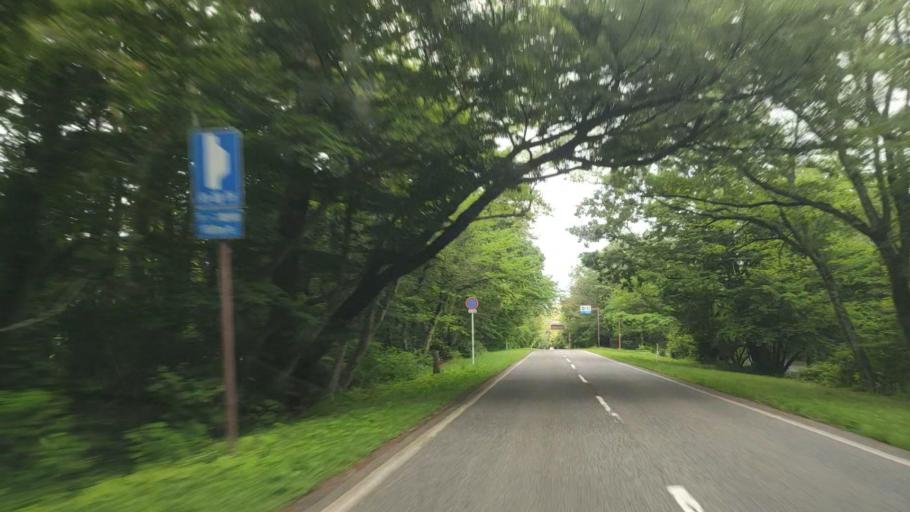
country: JP
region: Tottori
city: Yonago
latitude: 35.4009
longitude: 133.4937
